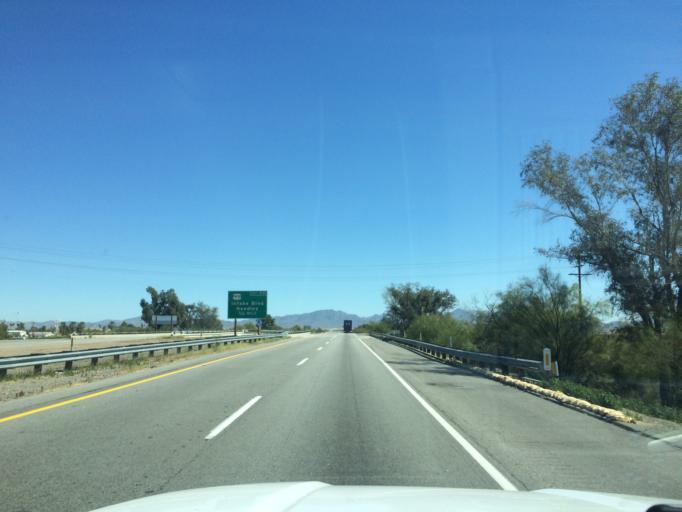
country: US
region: California
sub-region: Riverside County
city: Blythe
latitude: 33.6071
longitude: -114.5894
